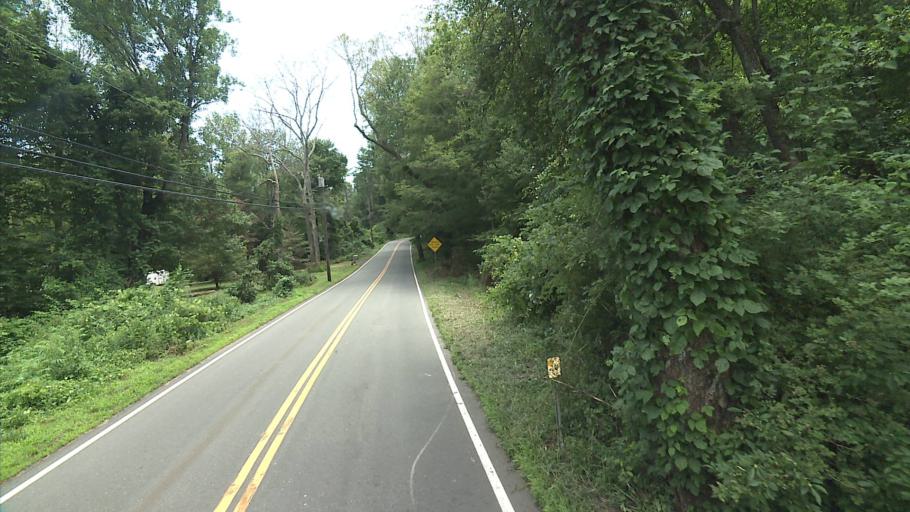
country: US
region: Connecticut
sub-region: New London County
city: Colchester
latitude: 41.4891
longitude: -72.3536
